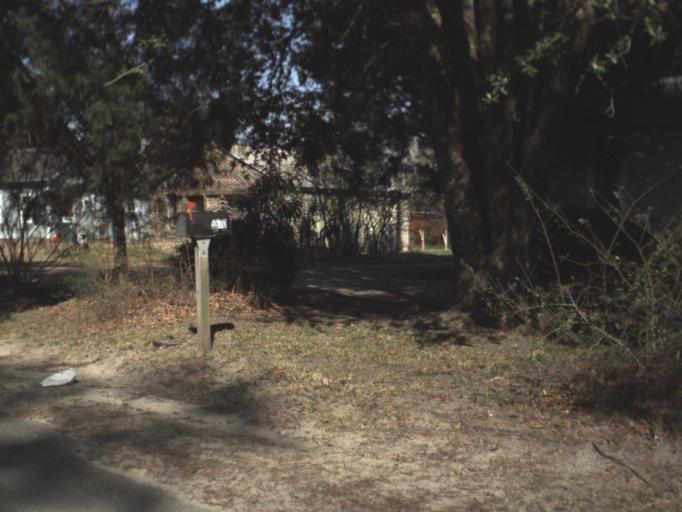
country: US
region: Florida
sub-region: Jackson County
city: Marianna
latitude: 30.7744
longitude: -85.2533
